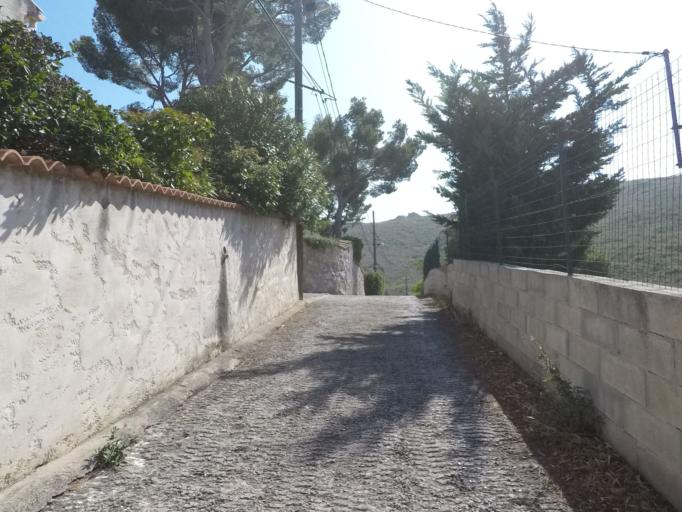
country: FR
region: Provence-Alpes-Cote d'Azur
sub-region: Departement des Bouches-du-Rhone
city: Marseille 09
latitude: 43.2552
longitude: 5.4392
